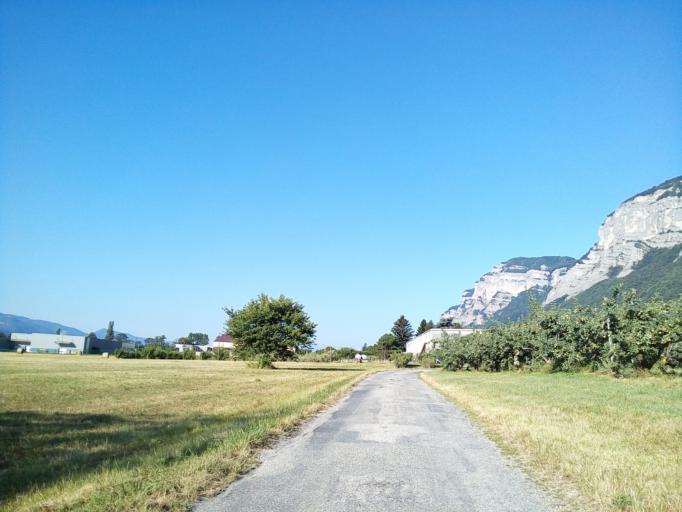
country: FR
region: Rhone-Alpes
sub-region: Departement de l'Isere
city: La Terrasse
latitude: 45.3164
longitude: 5.9271
